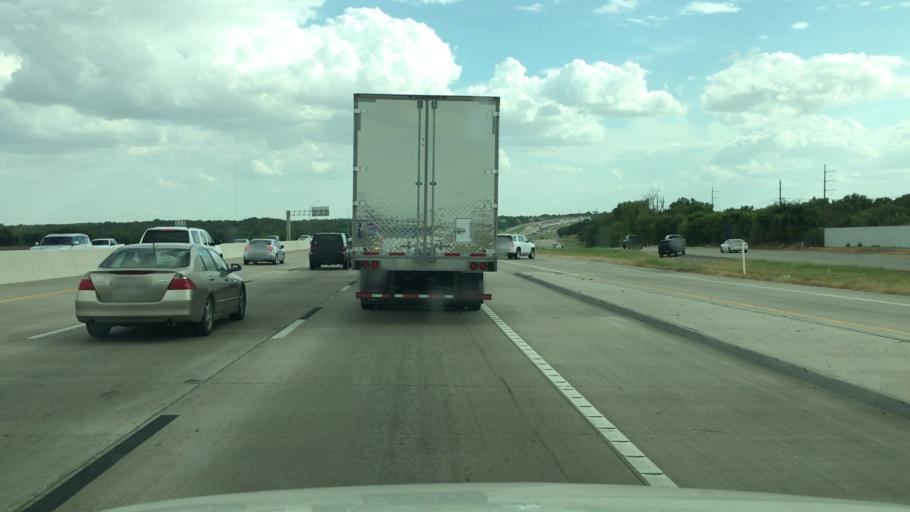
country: US
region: Texas
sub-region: McLennan County
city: Lorena
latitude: 31.3435
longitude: -97.2215
